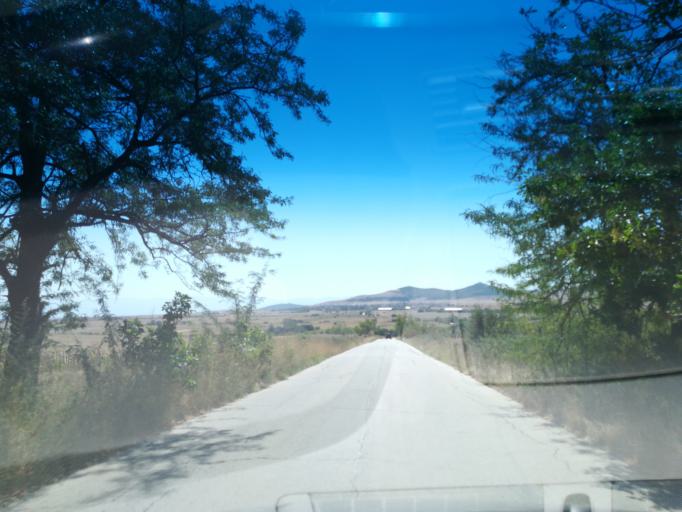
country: BG
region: Pazardzhik
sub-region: Obshtina Strelcha
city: Strelcha
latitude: 42.3616
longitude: 24.4017
